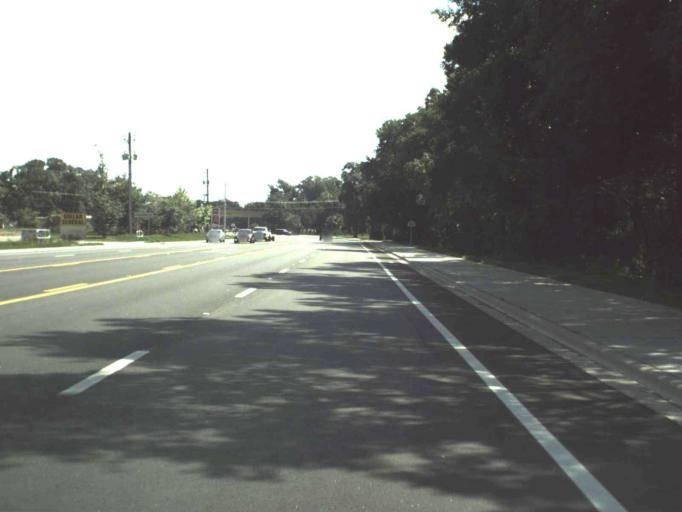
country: US
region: Florida
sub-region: Seminole County
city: Midway
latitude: 28.8434
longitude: -81.1648
